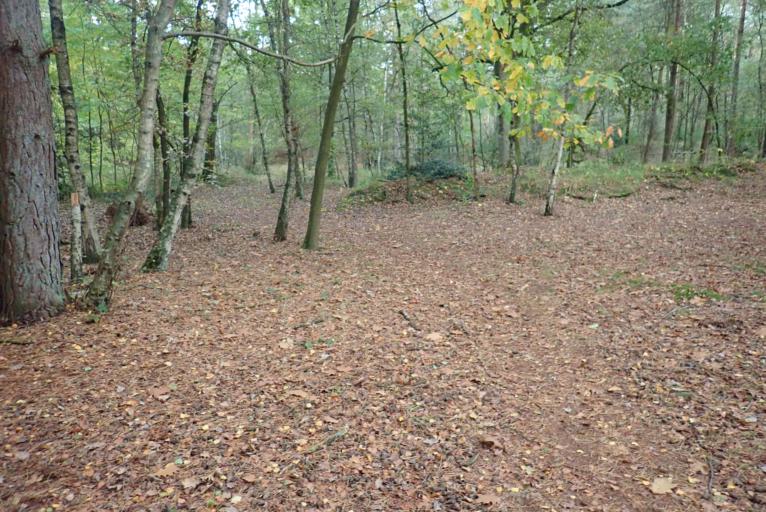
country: BE
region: Flanders
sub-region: Provincie Antwerpen
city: Essen
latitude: 51.4311
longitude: 4.4537
